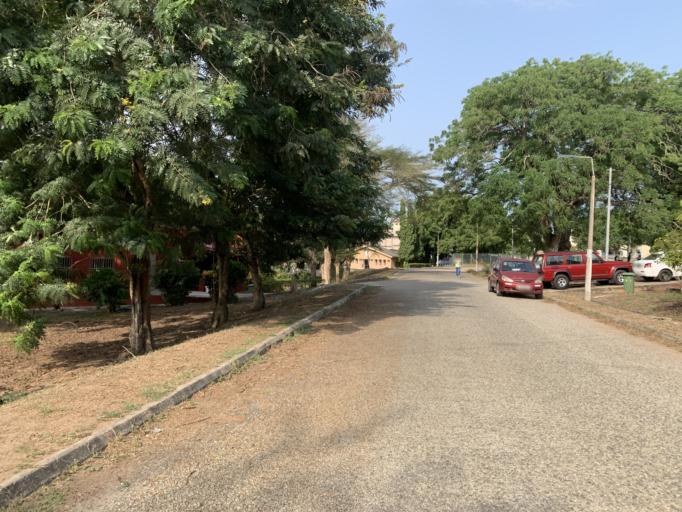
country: GH
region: Central
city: Winneba
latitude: 5.3386
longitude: -0.6282
